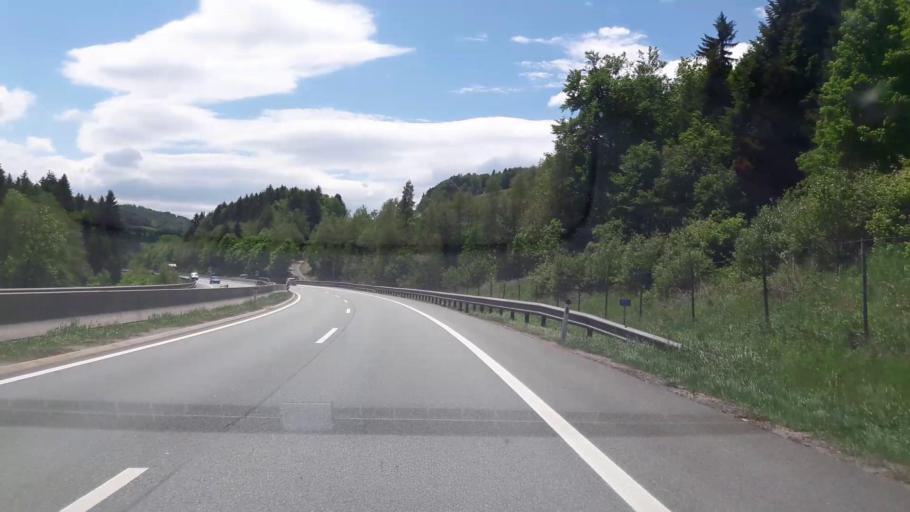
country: AT
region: Styria
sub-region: Politischer Bezirk Hartberg-Fuerstenfeld
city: Schaeffern
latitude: 47.4417
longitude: 16.0971
